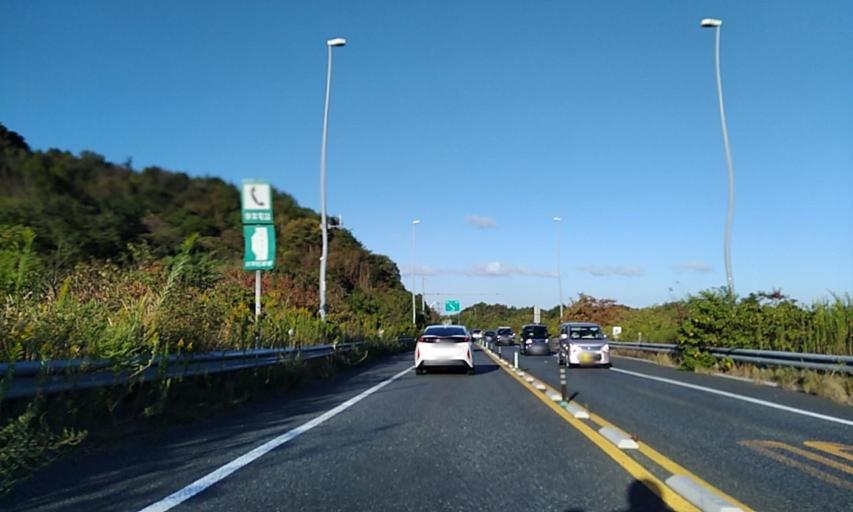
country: JP
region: Wakayama
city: Iwade
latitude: 34.3330
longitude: 135.2312
